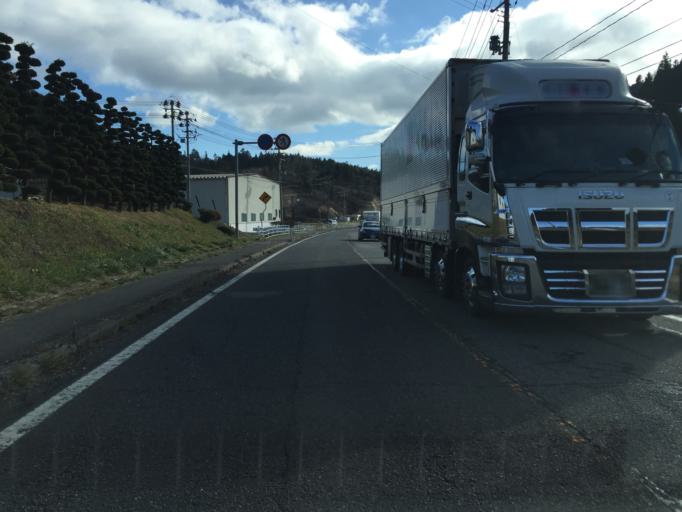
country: JP
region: Fukushima
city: Ishikawa
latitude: 37.2277
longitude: 140.5825
